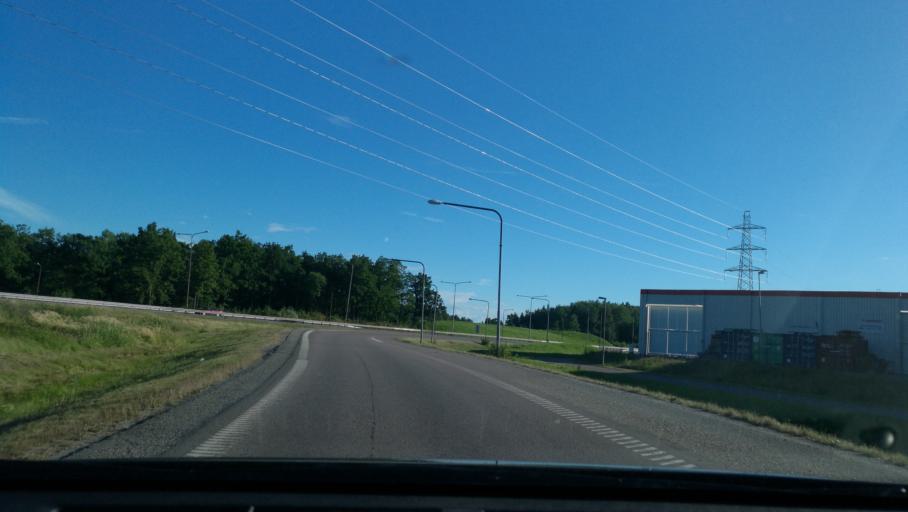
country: SE
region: Vaestmanland
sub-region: Vasteras
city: Vasteras
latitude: 59.6115
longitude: 16.4725
